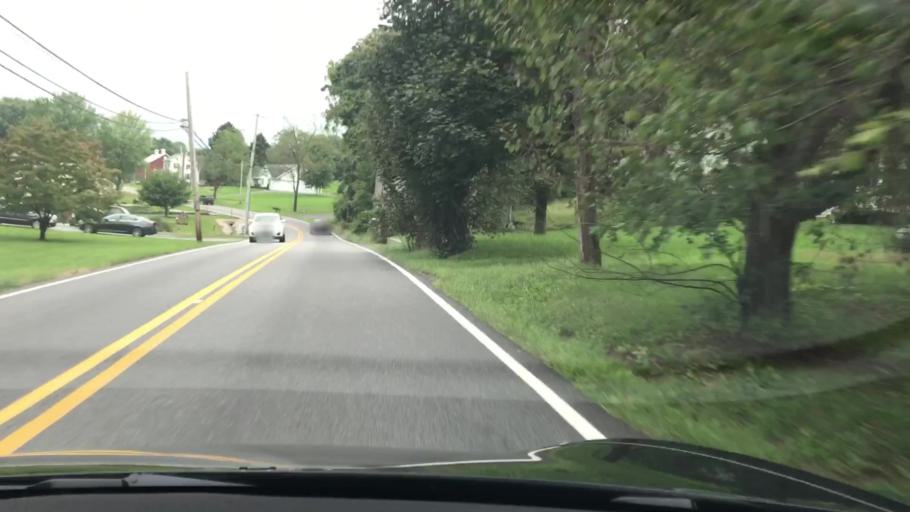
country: US
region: Pennsylvania
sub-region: York County
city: Dillsburg
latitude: 40.1022
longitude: -77.0598
